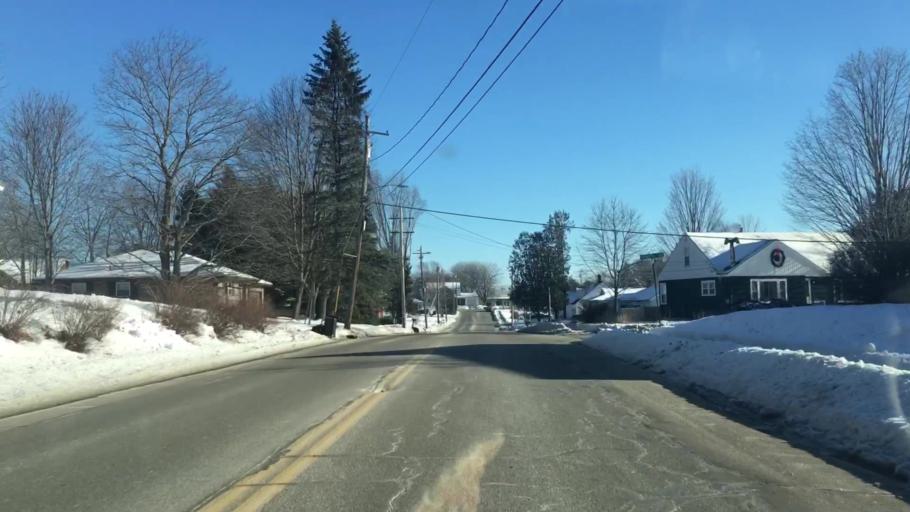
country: US
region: Maine
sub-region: Androscoggin County
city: Lewiston
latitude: 44.1051
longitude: -70.1763
